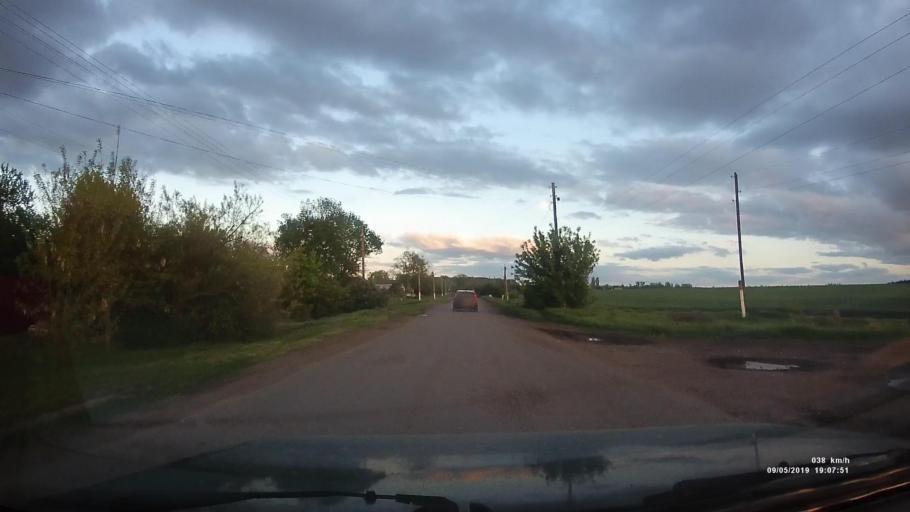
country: RU
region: Krasnodarskiy
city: Kanelovskaya
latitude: 46.7326
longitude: 39.1993
